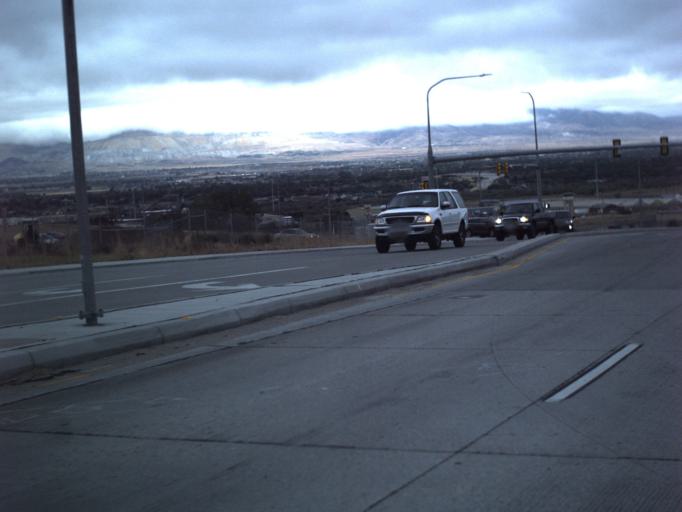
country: US
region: Utah
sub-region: Salt Lake County
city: Bluffdale
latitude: 40.4847
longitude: -111.8995
